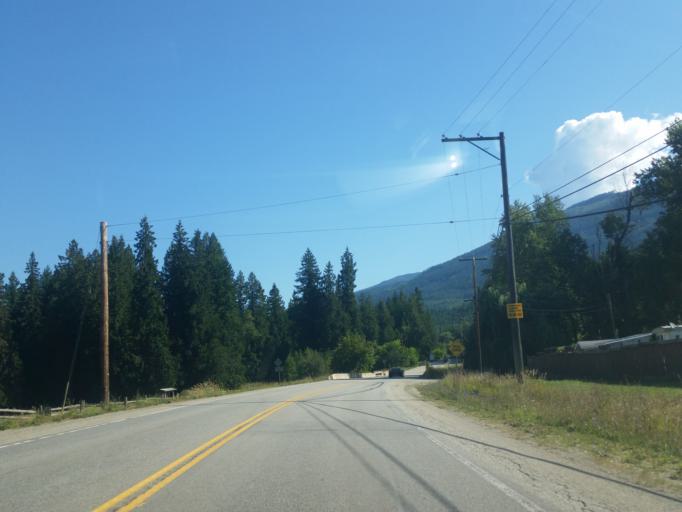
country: CA
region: British Columbia
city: Enderby
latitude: 50.6819
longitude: -119.0529
